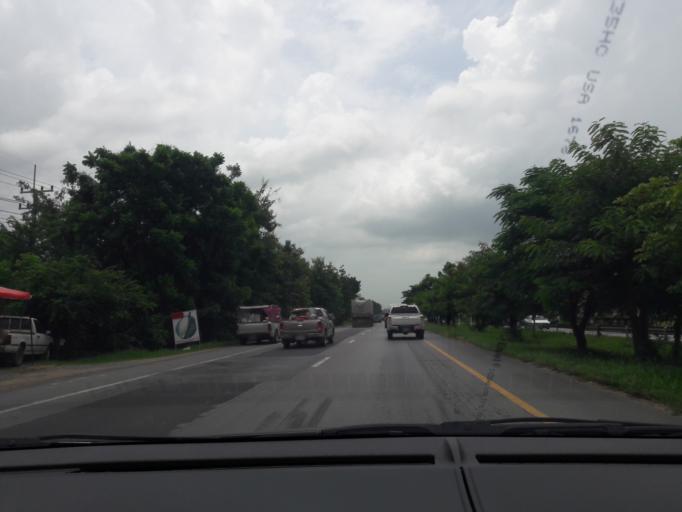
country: TH
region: Nakhon Ratchasima
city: Chaloem Phra Kiat
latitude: 15.0660
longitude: 102.1924
